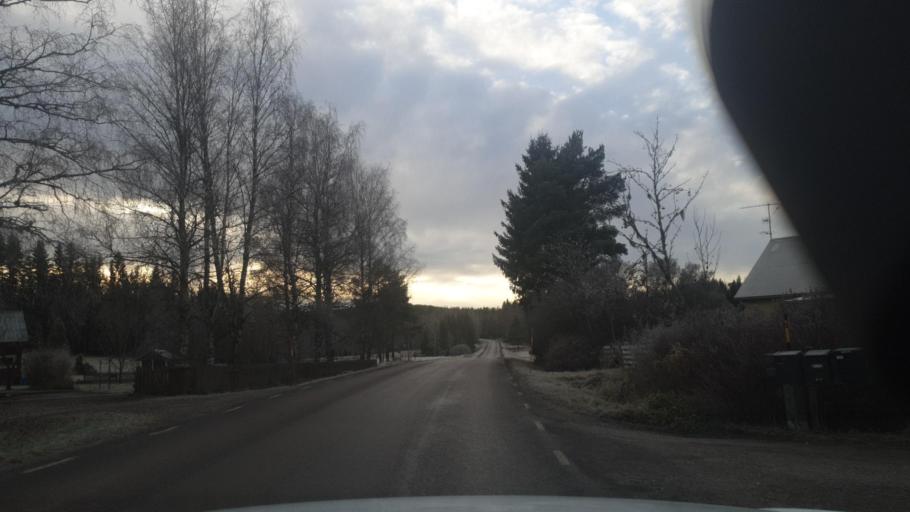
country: SE
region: Vaermland
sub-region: Eda Kommun
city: Amotfors
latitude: 59.8716
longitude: 12.5035
